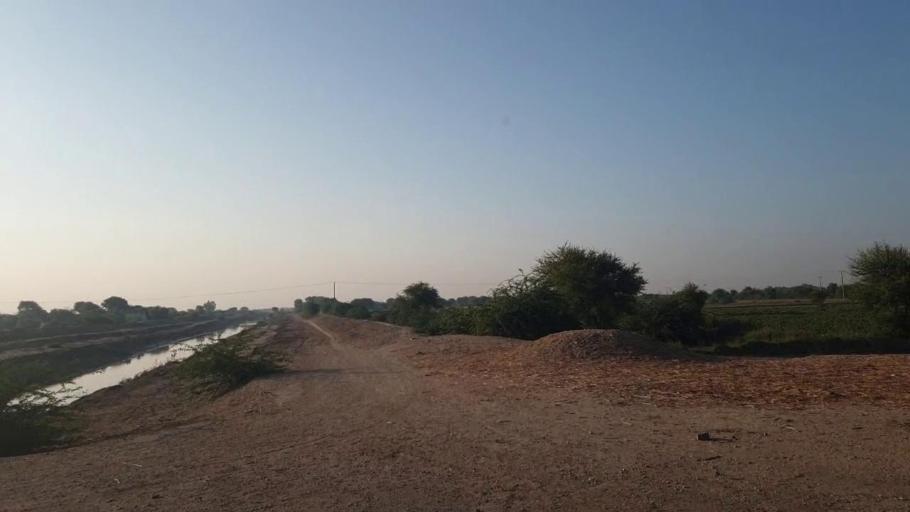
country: PK
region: Sindh
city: Badin
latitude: 24.6492
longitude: 68.7895
